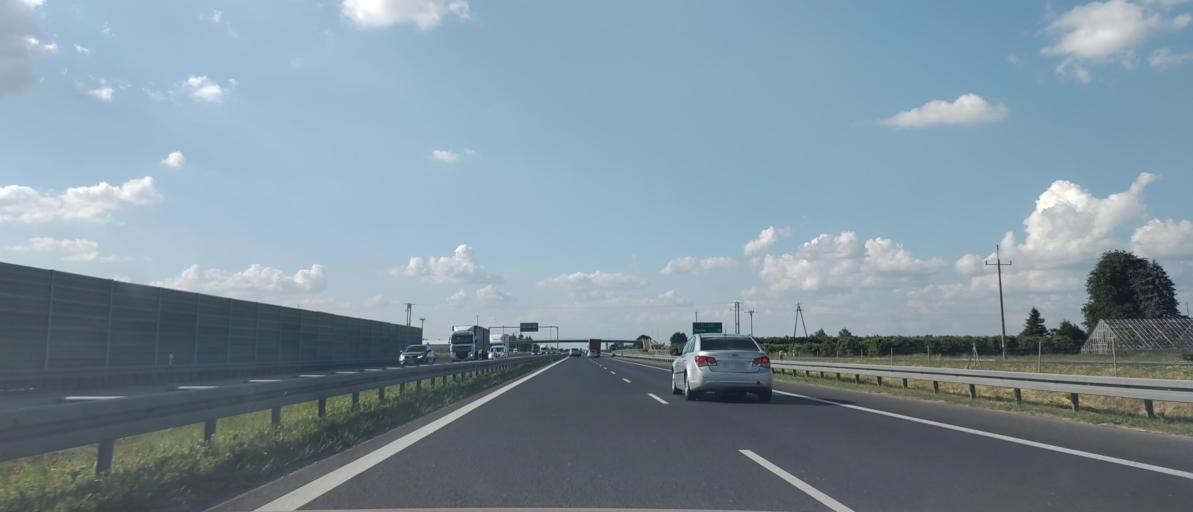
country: PL
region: Masovian Voivodeship
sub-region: Powiat grojecki
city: Goszczyn
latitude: 51.7640
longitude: 20.9052
